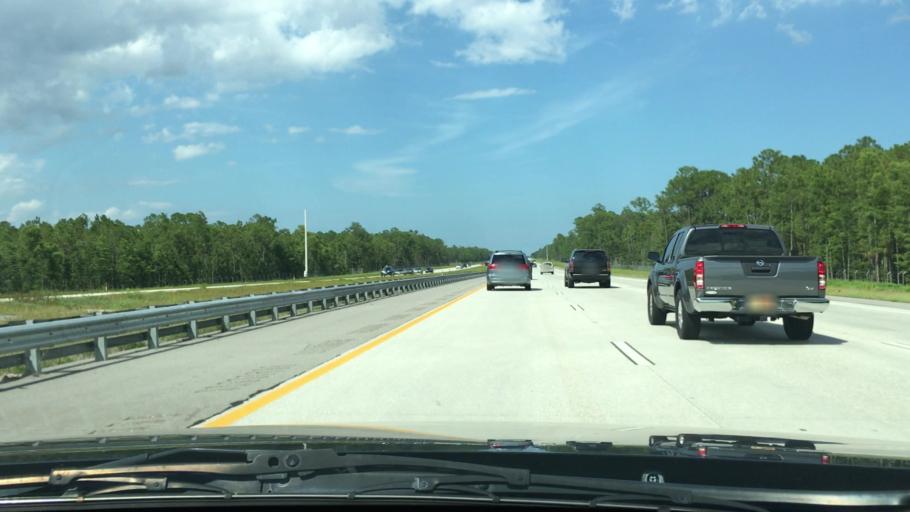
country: US
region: Florida
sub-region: Volusia County
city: Samsula-Spruce Creek
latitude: 29.1005
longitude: -81.1528
